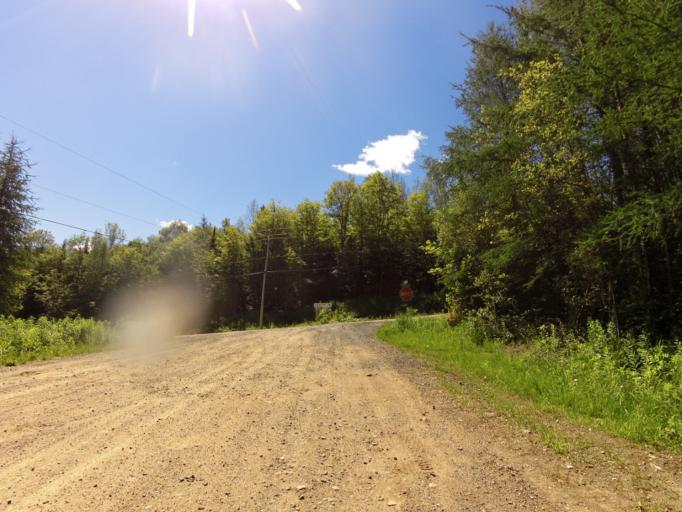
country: CA
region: Quebec
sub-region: Laurentides
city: Brownsburg-Chatham
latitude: 45.8384
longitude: -74.4756
